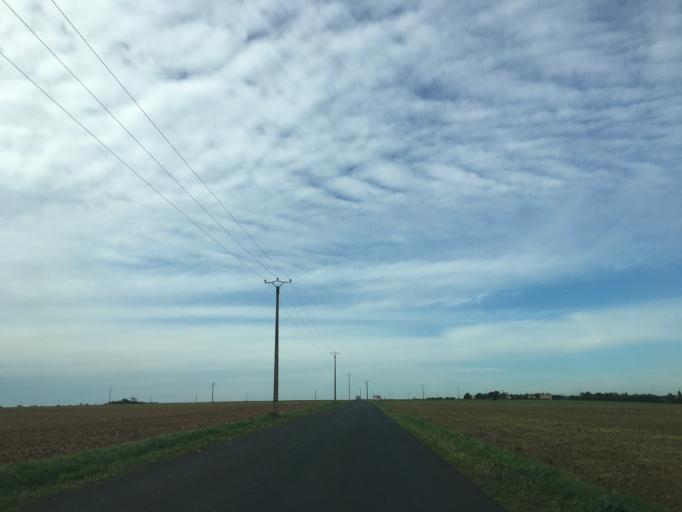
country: FR
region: Poitou-Charentes
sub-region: Departement des Deux-Sevres
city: Beauvoir-sur-Niort
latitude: 46.0710
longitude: -0.4945
